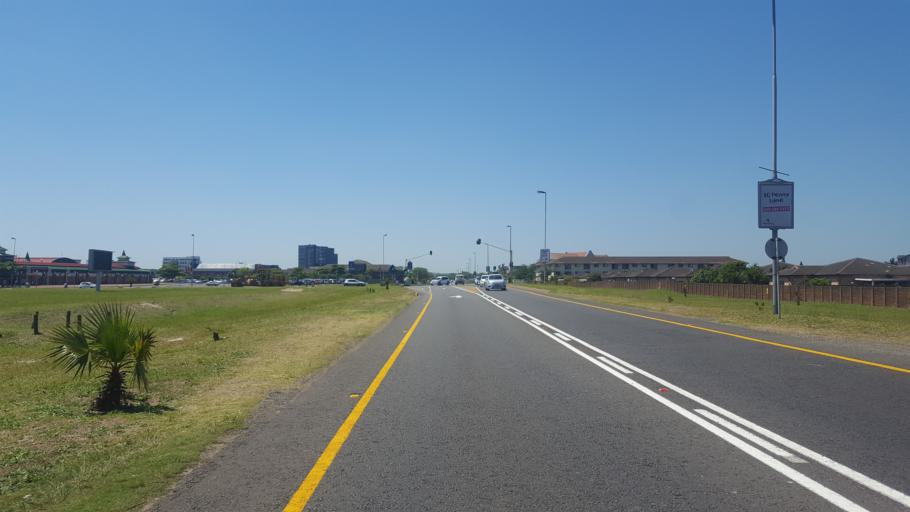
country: ZA
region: KwaZulu-Natal
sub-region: uThungulu District Municipality
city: Richards Bay
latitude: -28.7567
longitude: 32.0526
